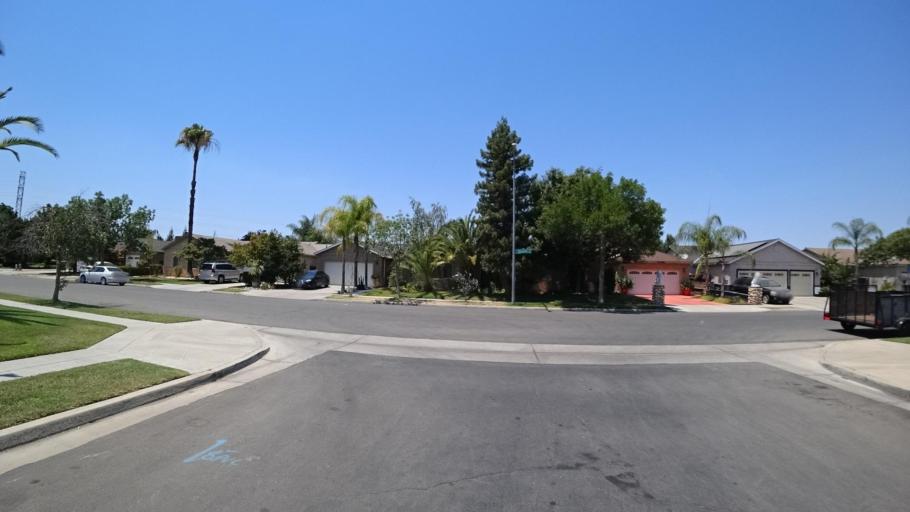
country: US
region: California
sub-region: Fresno County
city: Sunnyside
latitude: 36.7405
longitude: -119.6737
